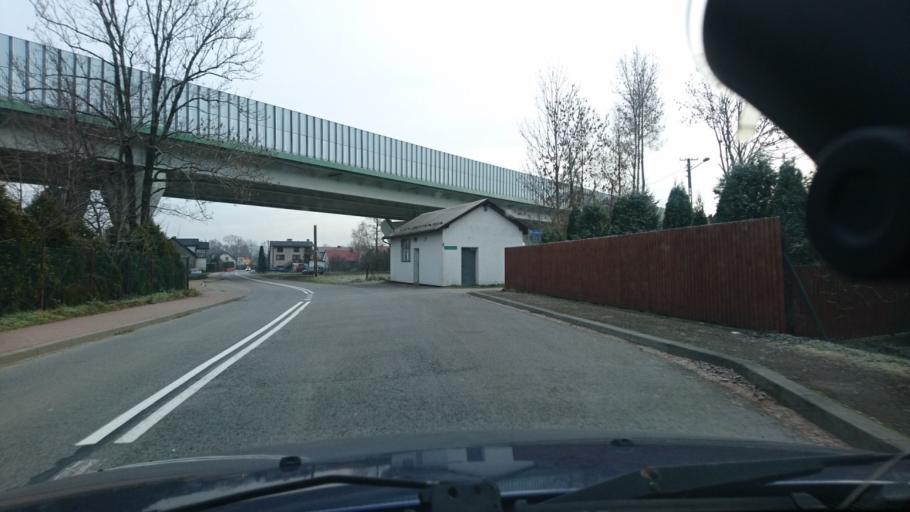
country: PL
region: Silesian Voivodeship
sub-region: Powiat bielski
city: Rybarzowice
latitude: 49.7282
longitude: 19.1167
